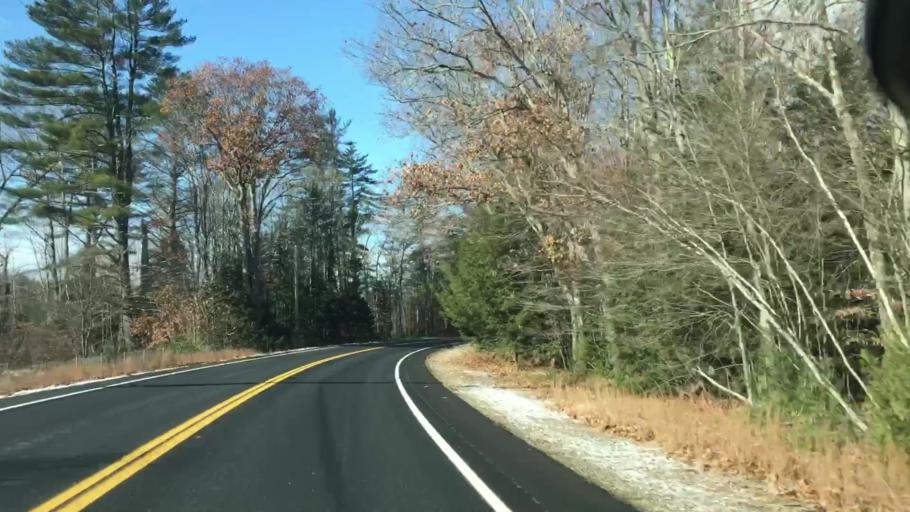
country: US
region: New Hampshire
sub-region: Carroll County
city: Effingham
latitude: 43.7886
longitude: -70.9745
